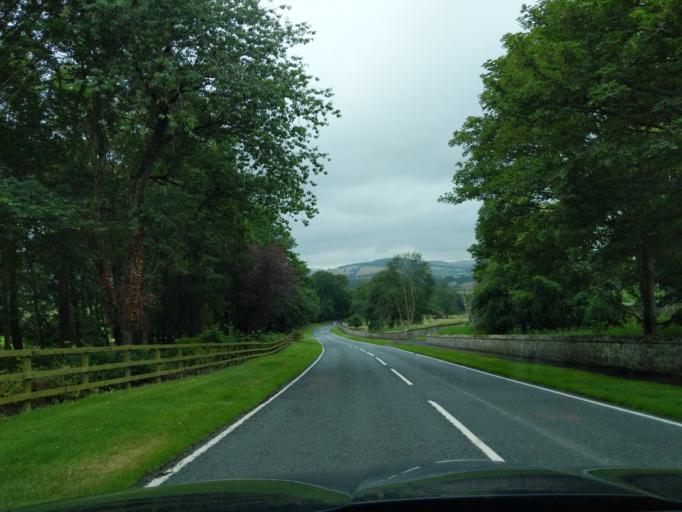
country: GB
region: England
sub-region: Northumberland
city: Ford
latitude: 55.6298
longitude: -2.0881
